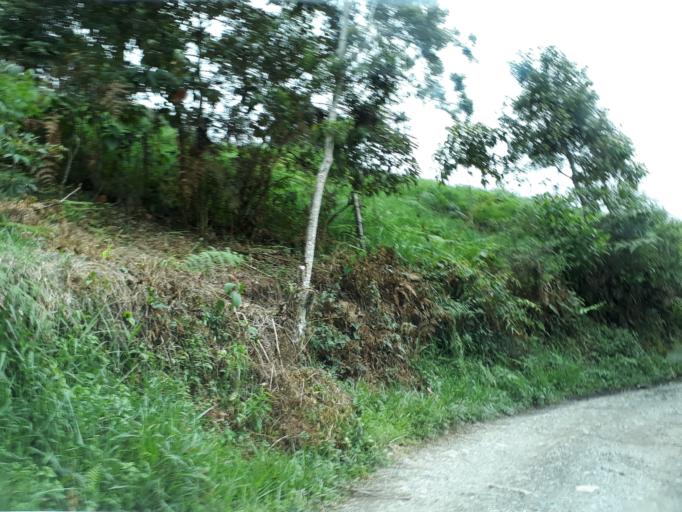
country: CO
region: Boyaca
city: Muzo
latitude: 5.3815
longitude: -74.0912
